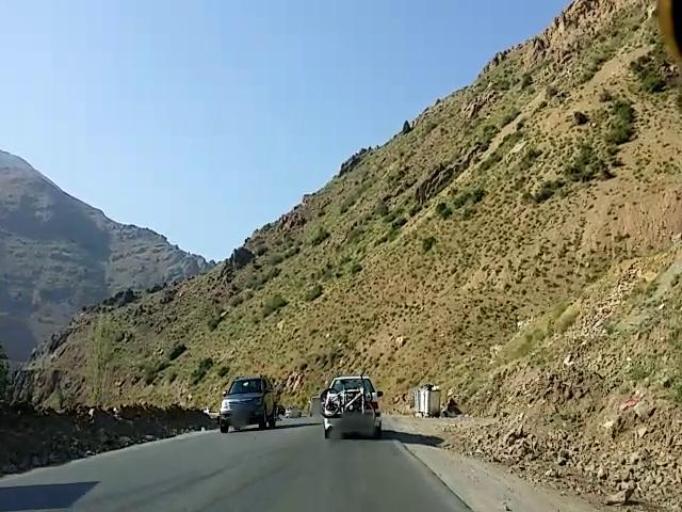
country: IR
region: Tehran
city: Tajrish
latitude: 36.0675
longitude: 51.3111
